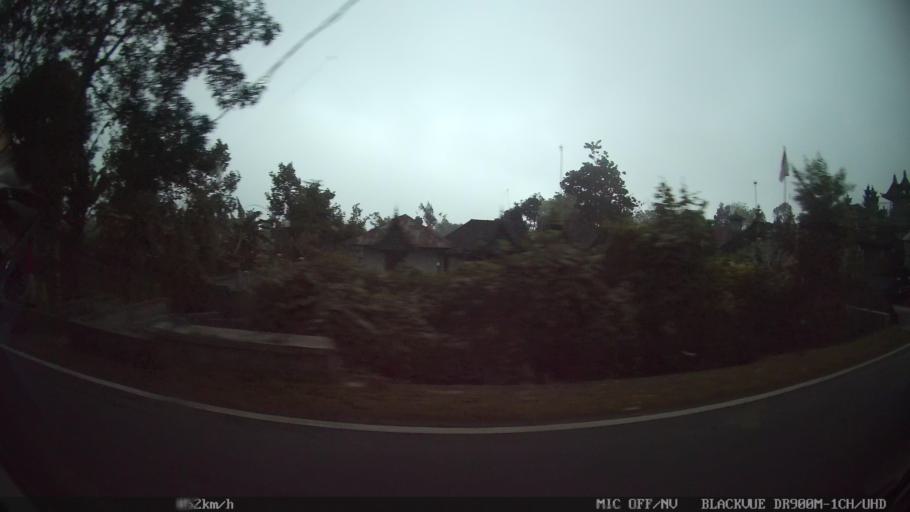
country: ID
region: Bali
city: Banjar Kedisan
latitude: -8.3078
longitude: 115.3054
